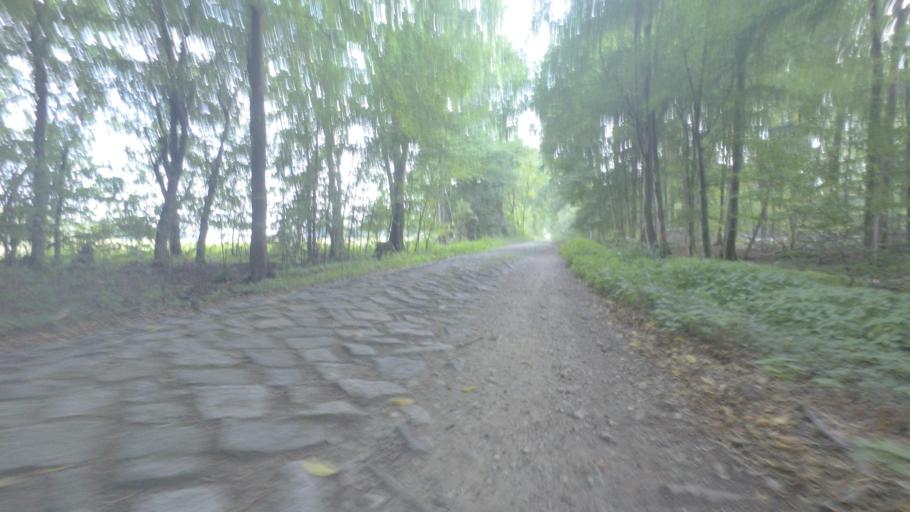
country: DE
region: Brandenburg
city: Wittstock
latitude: 53.2484
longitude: 12.4706
